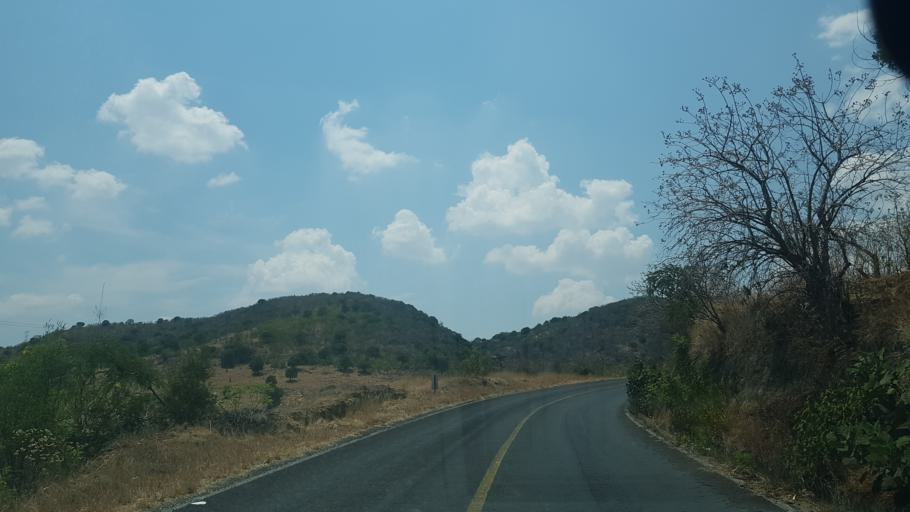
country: MX
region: Puebla
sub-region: Atzitzihuacan
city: Santiago Atzitzihuacan
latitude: 18.8334
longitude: -98.5985
